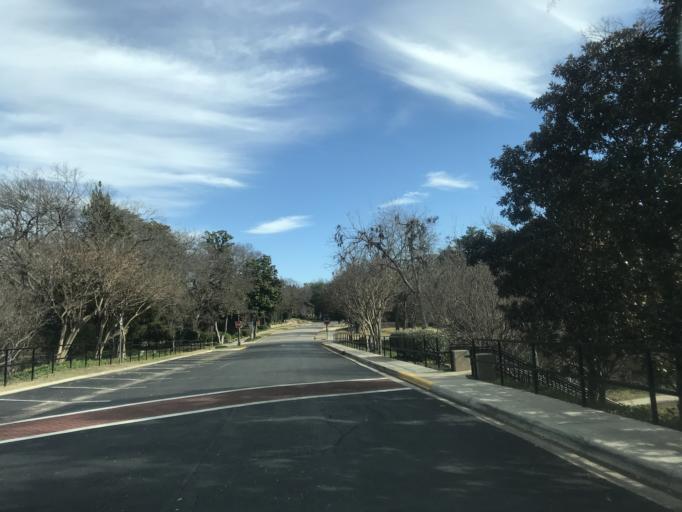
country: US
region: Texas
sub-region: Dallas County
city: Highland Park
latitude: 32.8267
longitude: -96.7979
